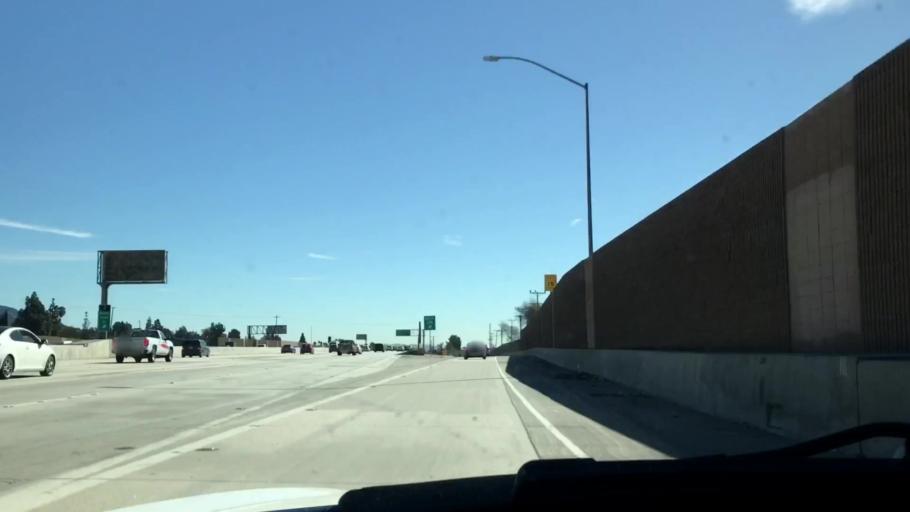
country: US
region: California
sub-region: Los Angeles County
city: North Hollywood
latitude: 34.2144
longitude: -118.3516
